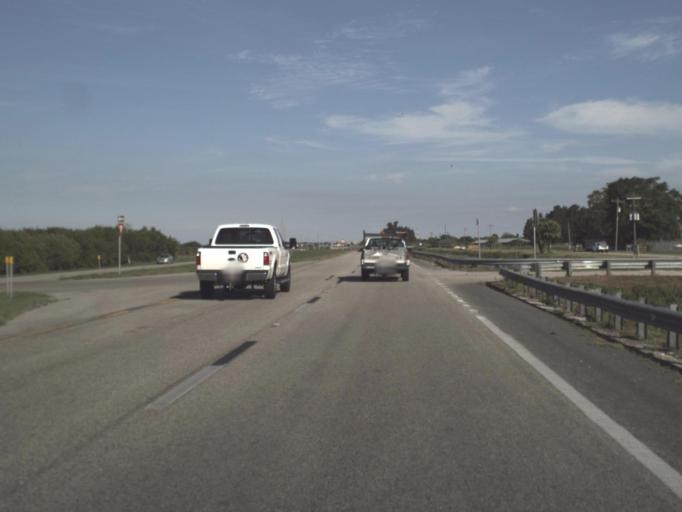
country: US
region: Florida
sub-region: Hendry County
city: Harlem
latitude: 26.7539
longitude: -80.9679
